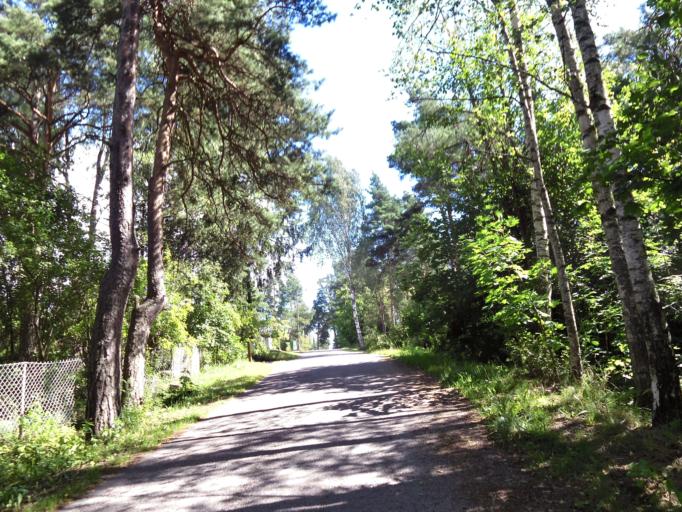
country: FI
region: Uusimaa
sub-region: Helsinki
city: Koukkuniemi
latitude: 60.1591
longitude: 24.7200
